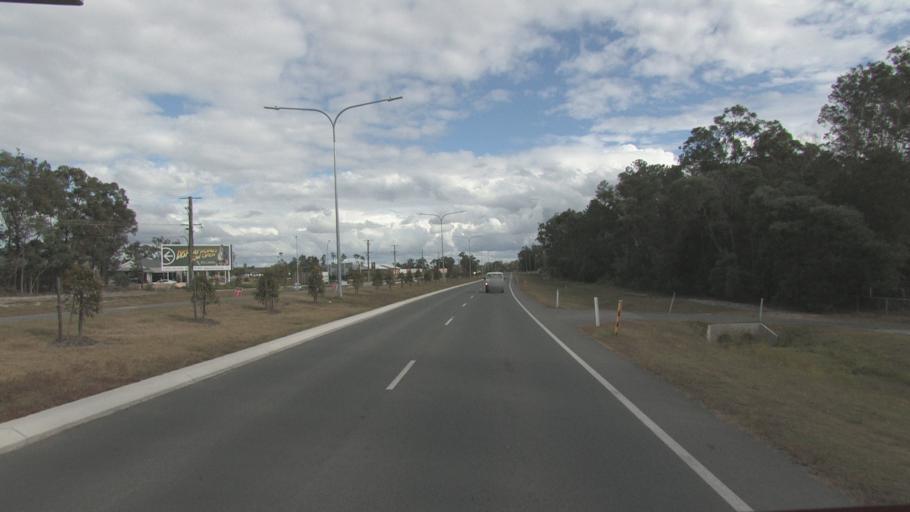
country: AU
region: Queensland
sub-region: Logan
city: Logan Reserve
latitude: -27.7026
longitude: 153.0973
